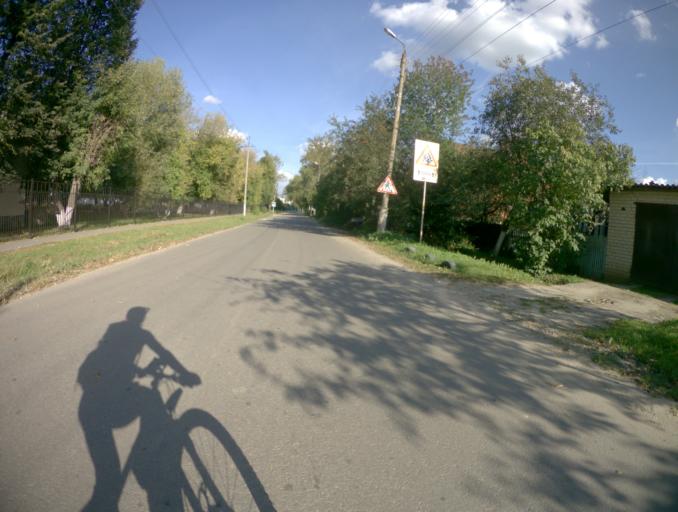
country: RU
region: Vladimir
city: Petushki
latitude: 55.9283
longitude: 39.4605
